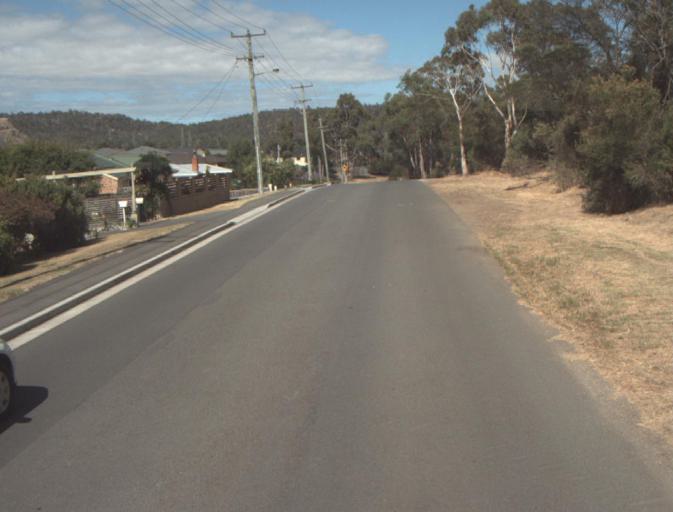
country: AU
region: Tasmania
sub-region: Launceston
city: Summerhill
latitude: -41.4719
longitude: 147.1180
